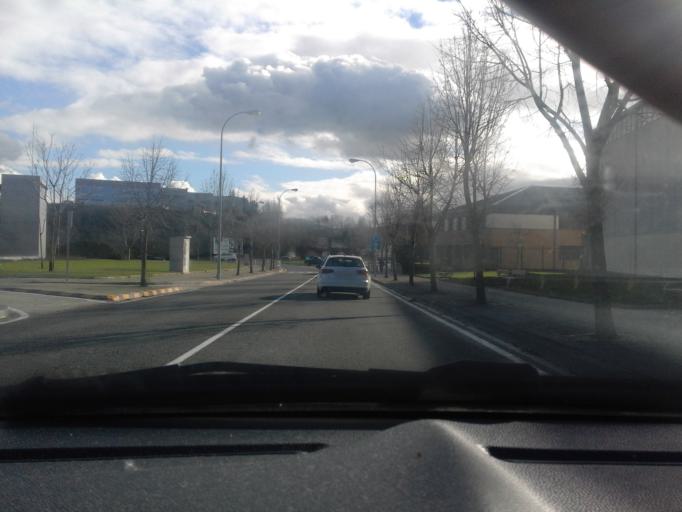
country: ES
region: Navarre
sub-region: Provincia de Navarra
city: Burlata
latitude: 42.8260
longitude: -1.6111
